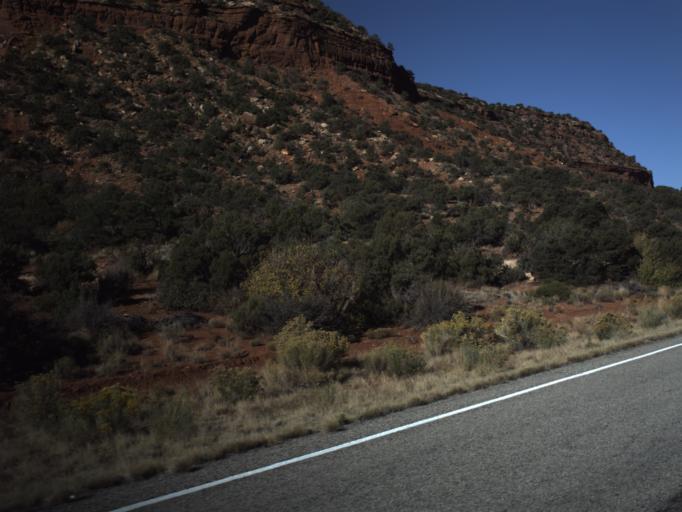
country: US
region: Utah
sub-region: San Juan County
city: Blanding
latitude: 37.6005
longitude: -110.0568
